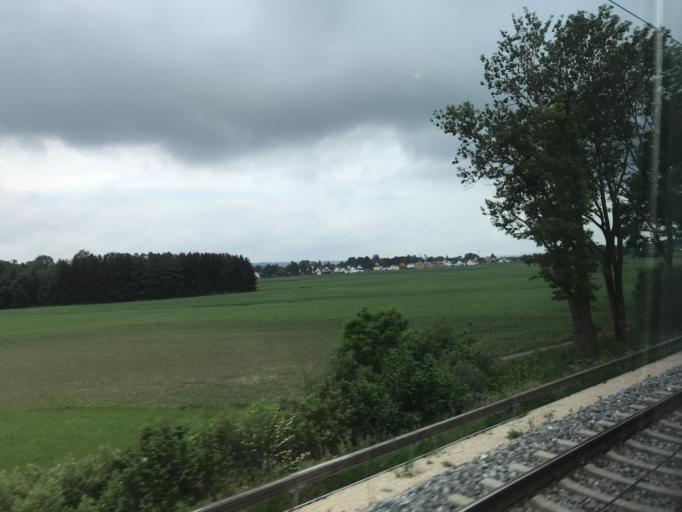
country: DE
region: Bavaria
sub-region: Swabia
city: Ustersbach
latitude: 48.3298
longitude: 10.6654
